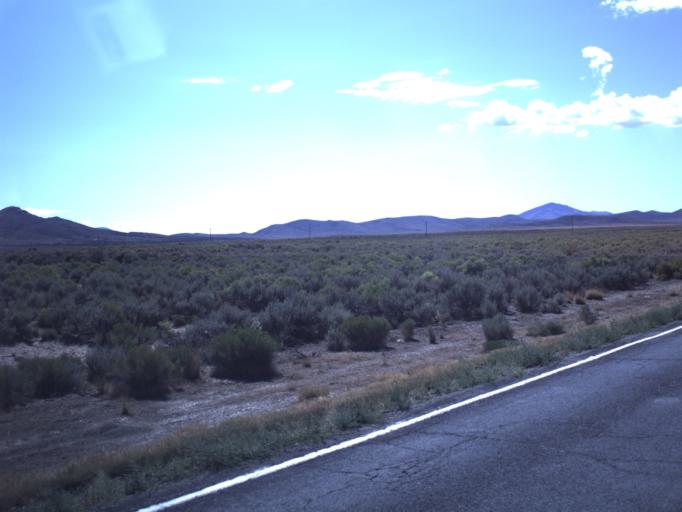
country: US
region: Utah
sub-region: Tooele County
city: Tooele
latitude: 40.1229
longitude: -112.4308
